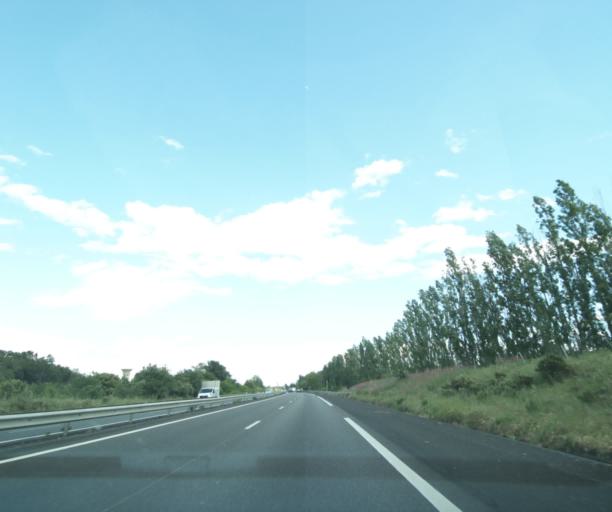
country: FR
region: Languedoc-Roussillon
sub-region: Departement du Gard
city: Garons
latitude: 43.7426
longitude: 4.4456
